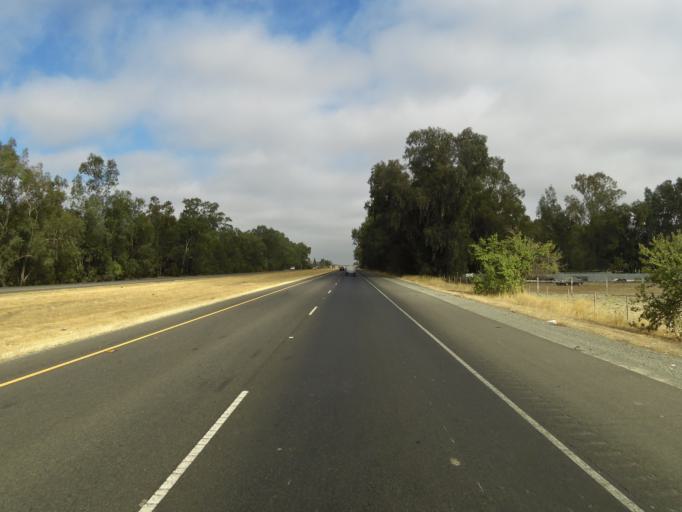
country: US
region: California
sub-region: Yolo County
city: Dunnigan
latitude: 38.8977
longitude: -121.9817
